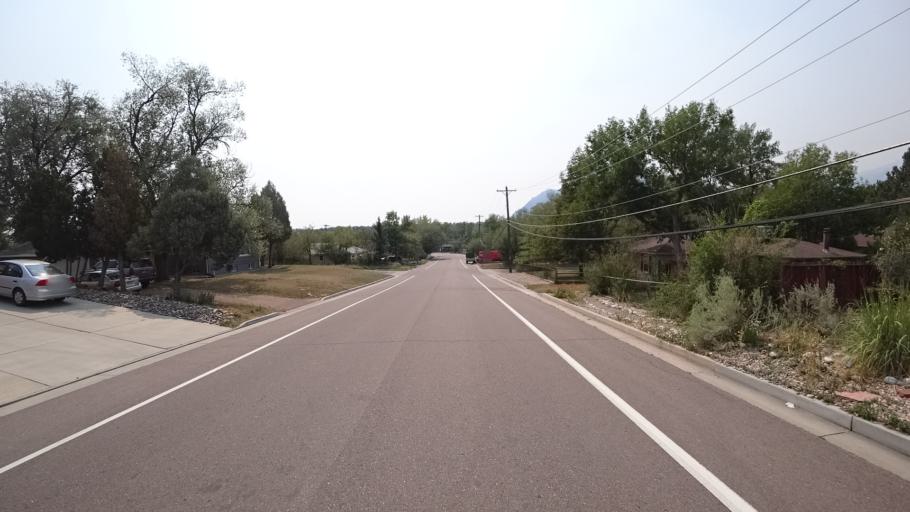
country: US
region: Colorado
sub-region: El Paso County
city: Colorado Springs
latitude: 38.8111
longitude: -104.8351
